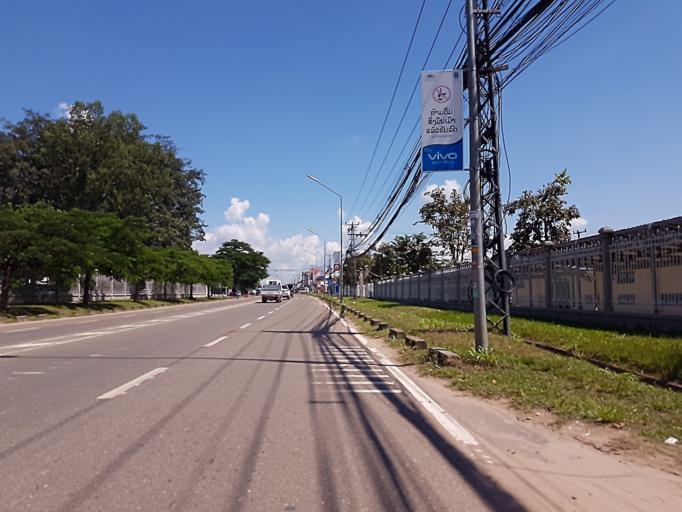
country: TH
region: Nong Khai
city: Si Chiang Mai
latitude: 17.9013
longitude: 102.6322
